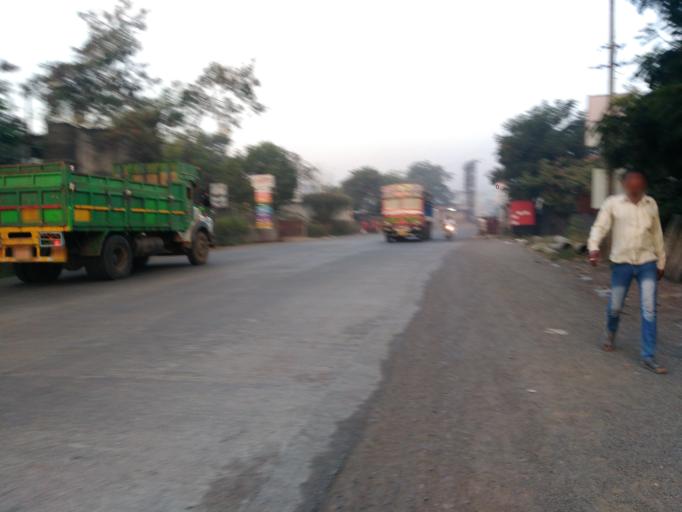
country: IN
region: Maharashtra
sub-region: Pune Division
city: Pune
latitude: 18.4517
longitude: 73.8924
